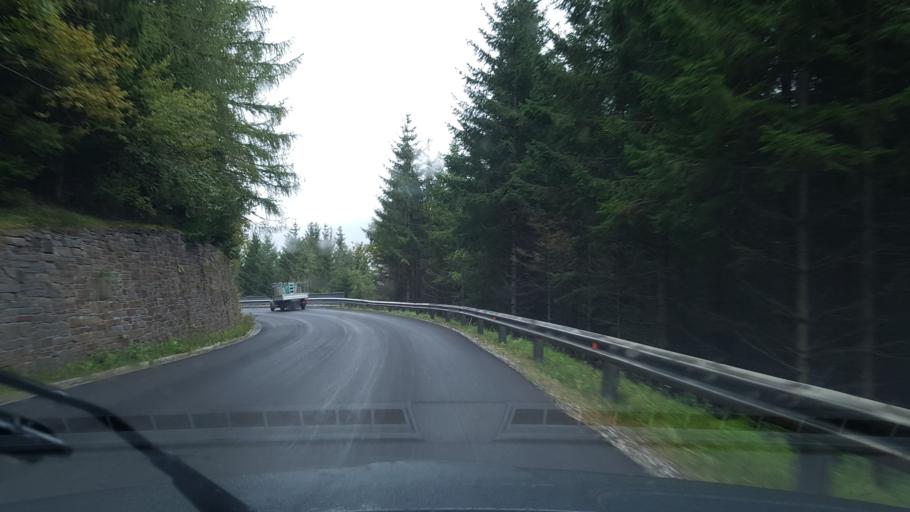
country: AT
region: Styria
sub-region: Politischer Bezirk Voitsberg
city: Salla
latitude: 47.1075
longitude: 14.9368
